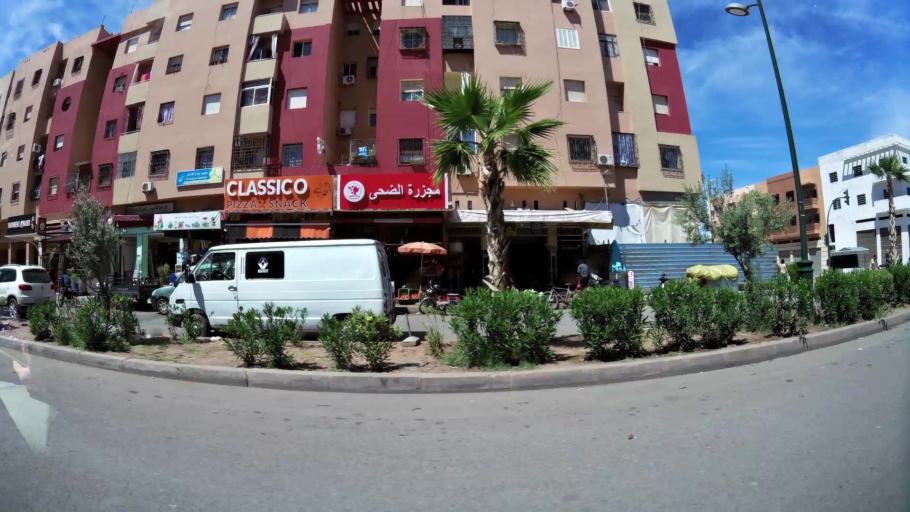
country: MA
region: Marrakech-Tensift-Al Haouz
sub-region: Marrakech
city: Marrakesh
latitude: 31.6401
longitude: -8.0745
